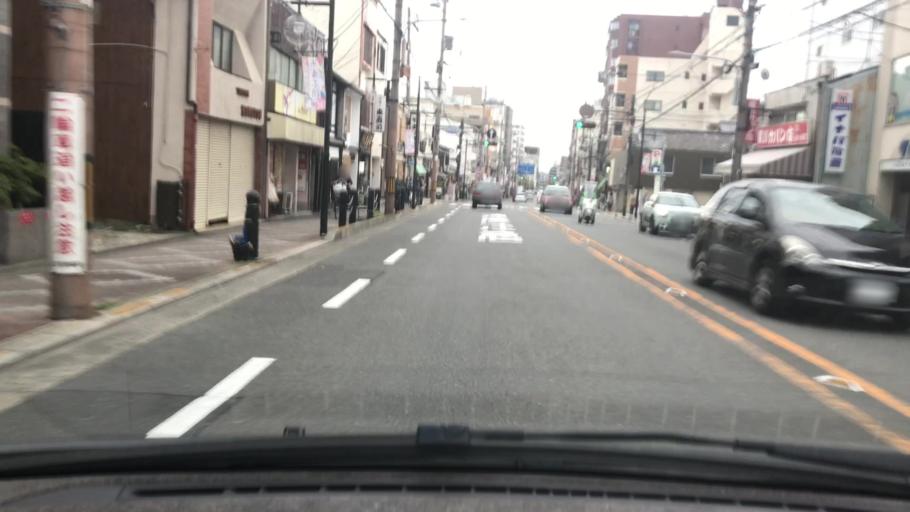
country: JP
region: Kyoto
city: Kyoto
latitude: 35.0206
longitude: 135.7426
